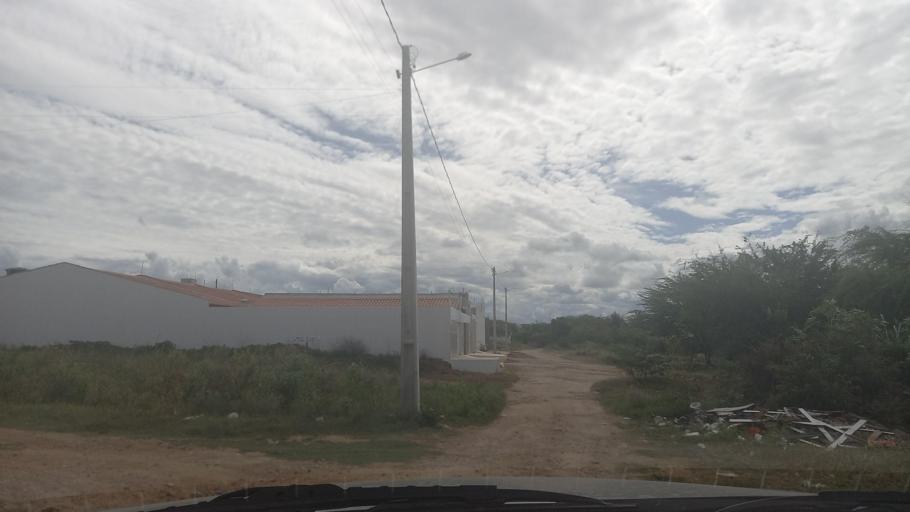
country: BR
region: Pernambuco
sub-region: Caruaru
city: Caruaru
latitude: -8.2911
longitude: -35.9886
